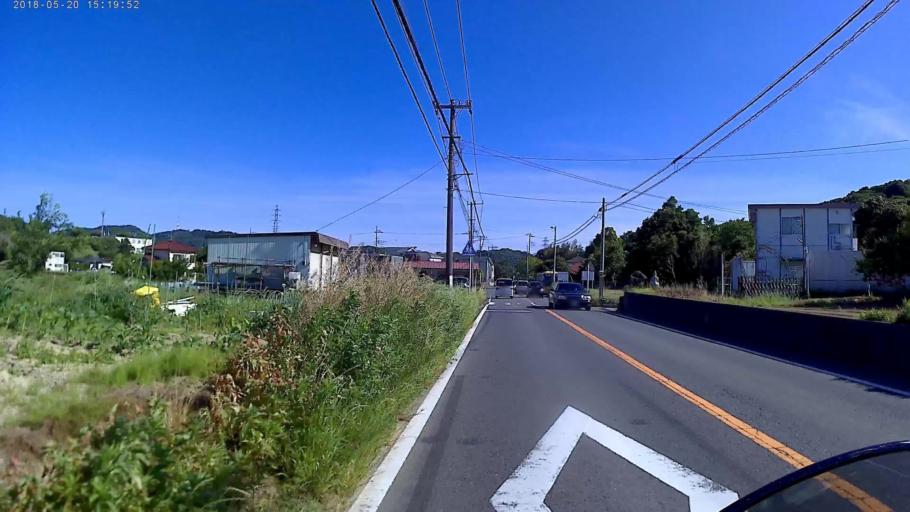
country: JP
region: Kanagawa
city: Oiso
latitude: 35.3387
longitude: 139.2928
